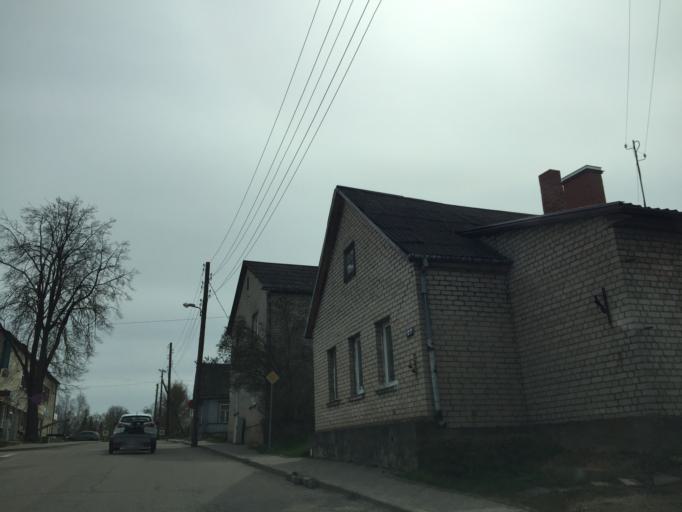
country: LV
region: Ludzas Rajons
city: Ludza
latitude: 56.5453
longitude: 27.7203
